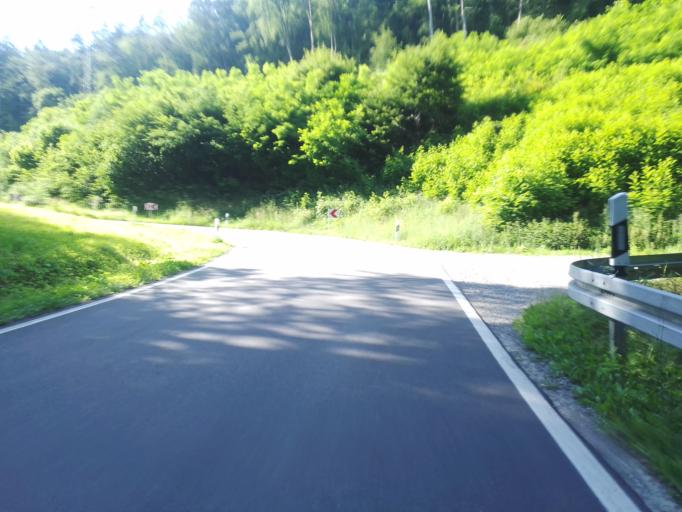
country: DE
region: Bavaria
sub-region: Regierungsbezirk Unterfranken
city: Hasloch
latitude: 49.7963
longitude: 9.4905
